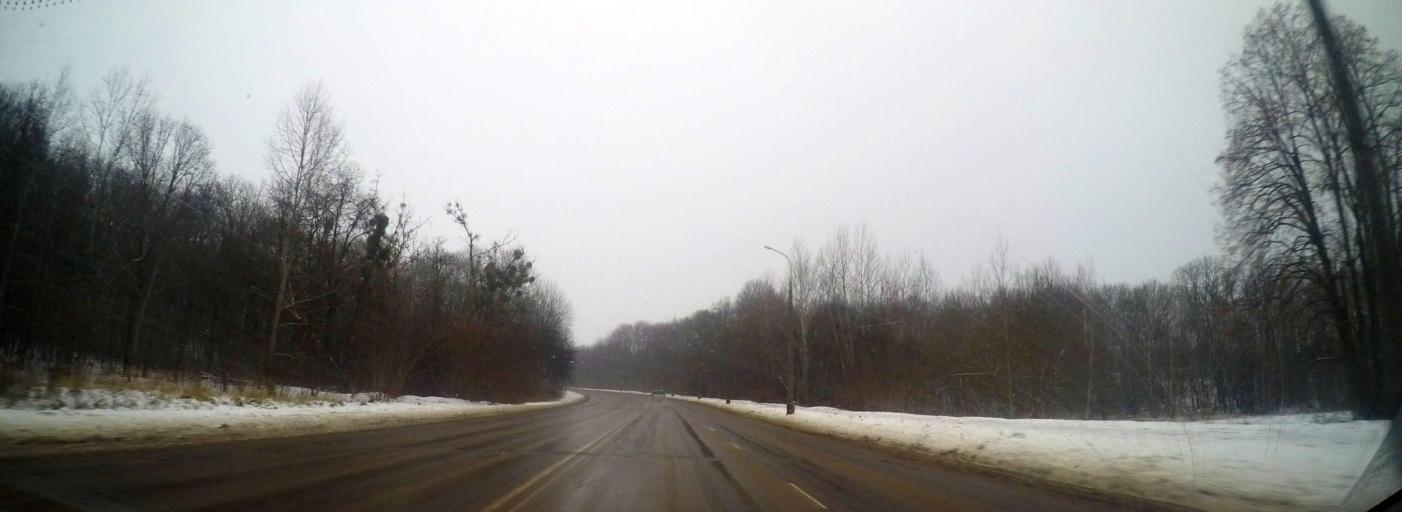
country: BY
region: Grodnenskaya
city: Hrodna
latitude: 53.6807
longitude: 23.8826
